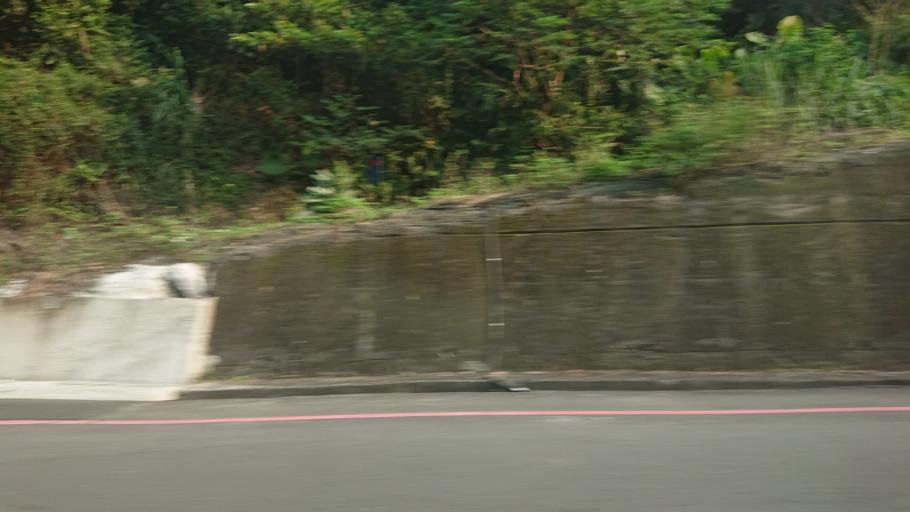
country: TW
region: Taiwan
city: Daxi
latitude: 24.8626
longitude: 121.4229
